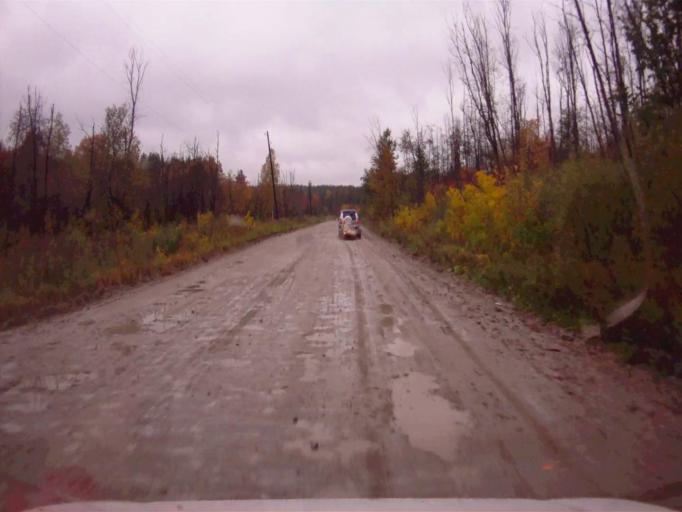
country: RU
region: Chelyabinsk
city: Kyshtym
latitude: 55.7377
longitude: 60.5128
